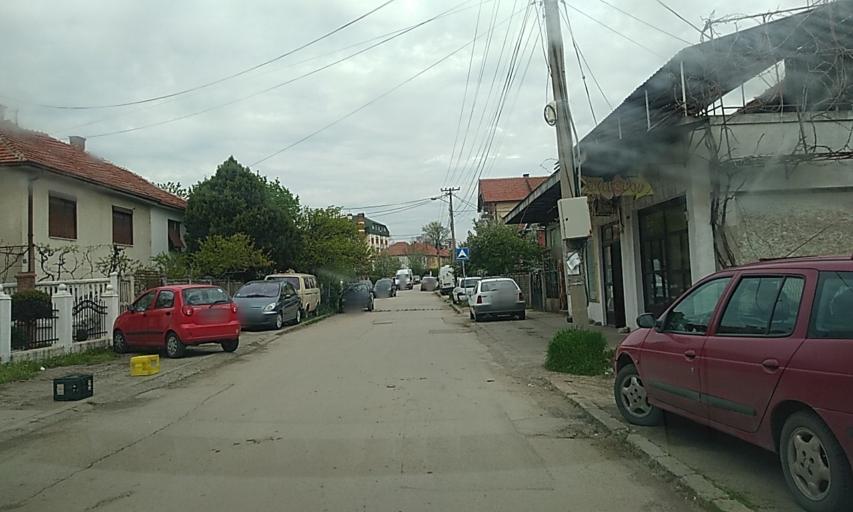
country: RS
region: Central Serbia
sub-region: Nisavski Okrug
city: Nis
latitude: 43.3303
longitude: 21.9105
